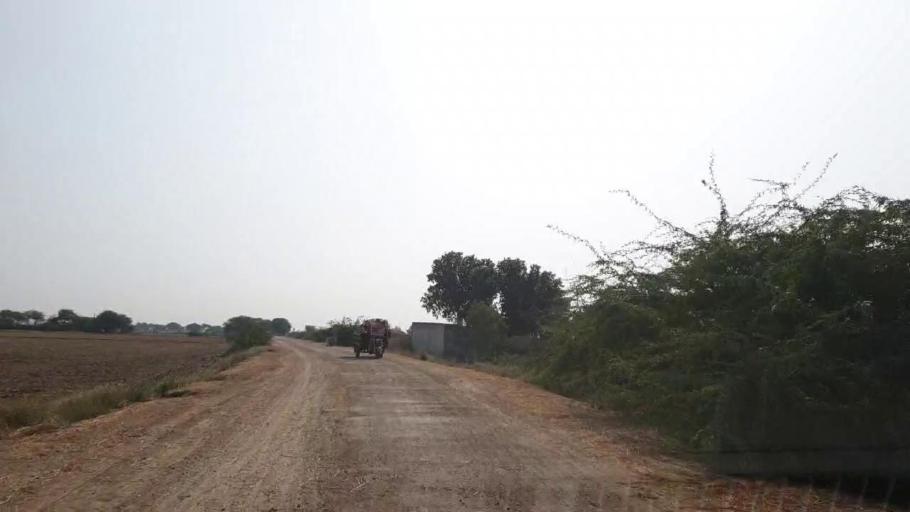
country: PK
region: Sindh
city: Matli
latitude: 24.9861
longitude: 68.5800
